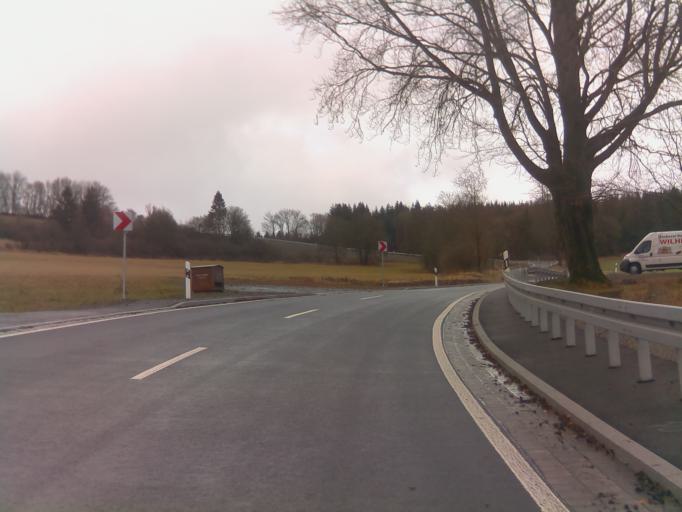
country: DE
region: Thuringia
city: Unterweid
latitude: 50.6087
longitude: 10.0739
